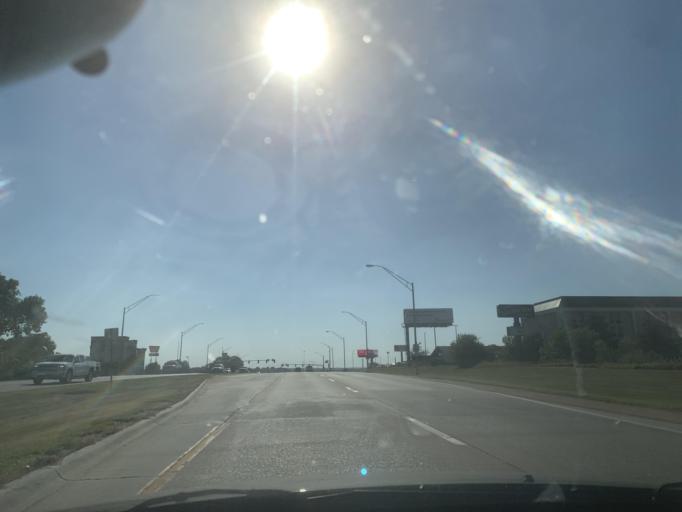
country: US
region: Nebraska
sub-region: Douglas County
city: Ralston
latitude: 41.2127
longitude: -96.0784
